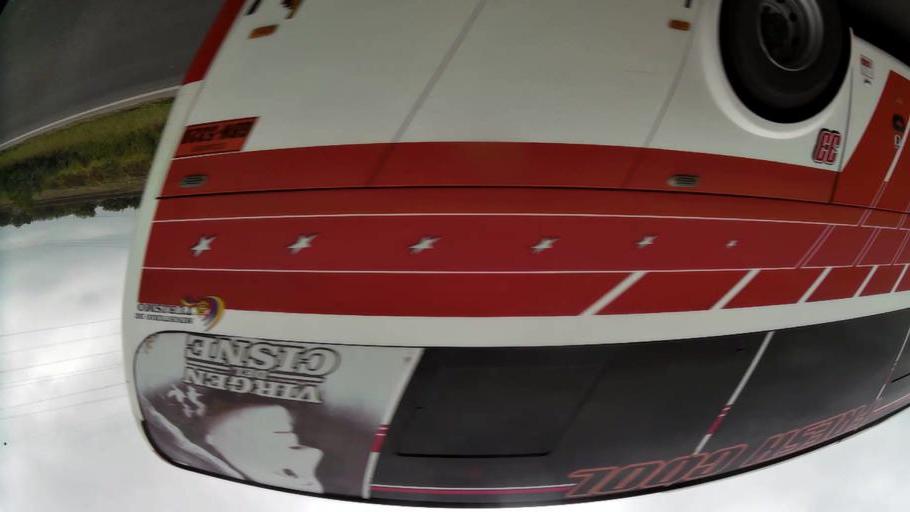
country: EC
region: Guayas
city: Yaguachi Nuevo
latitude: -2.2967
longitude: -79.6390
